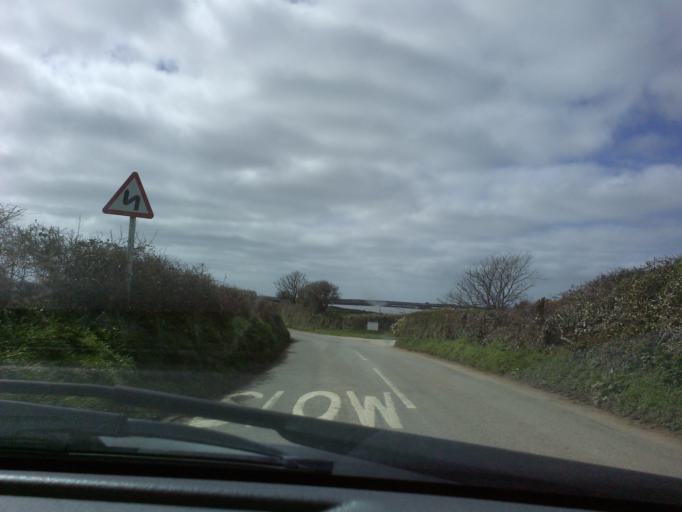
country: GB
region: England
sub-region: Cornwall
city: St. Buryan
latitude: 50.0621
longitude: -5.6029
